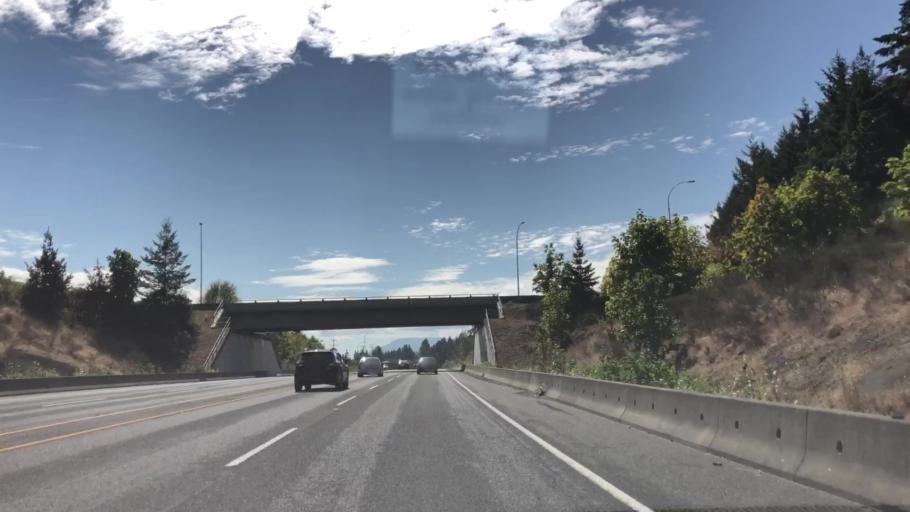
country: CA
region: British Columbia
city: Nanaimo
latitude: 49.1265
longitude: -123.8637
